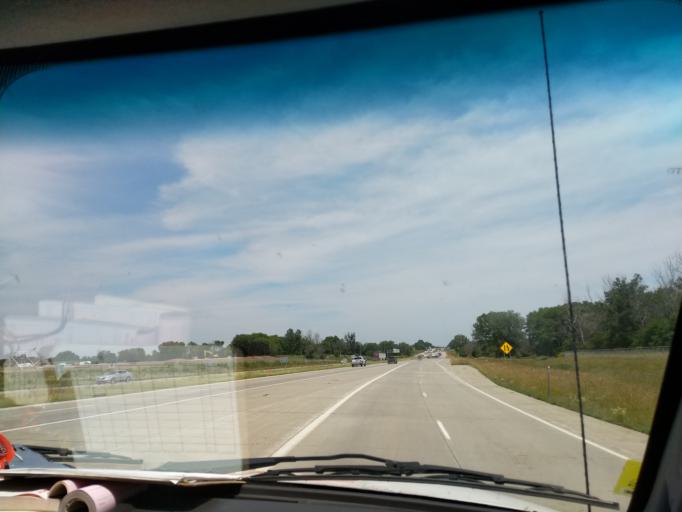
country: US
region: Iowa
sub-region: Dallas County
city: Waukee
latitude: 41.5709
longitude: -93.8498
